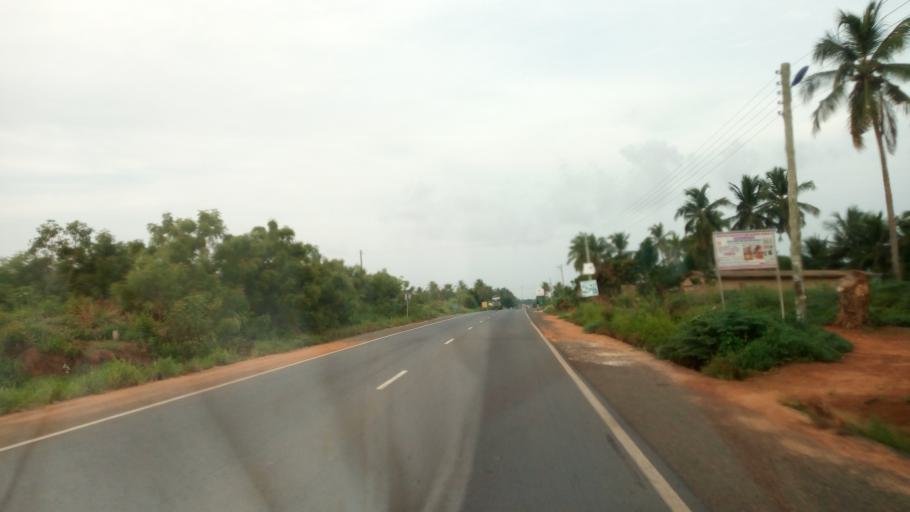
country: TG
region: Maritime
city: Lome
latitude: 6.0857
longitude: 1.0605
